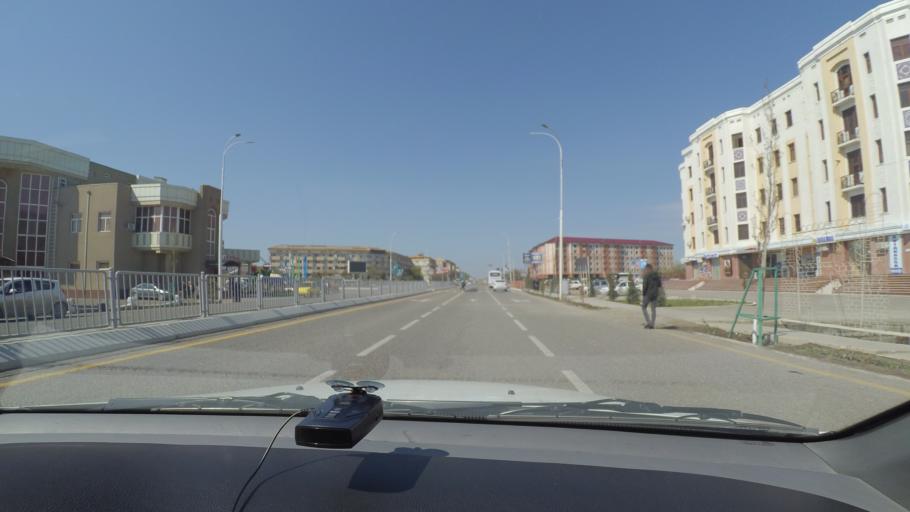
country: UZ
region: Bukhara
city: Bukhara
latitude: 39.7679
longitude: 64.4583
